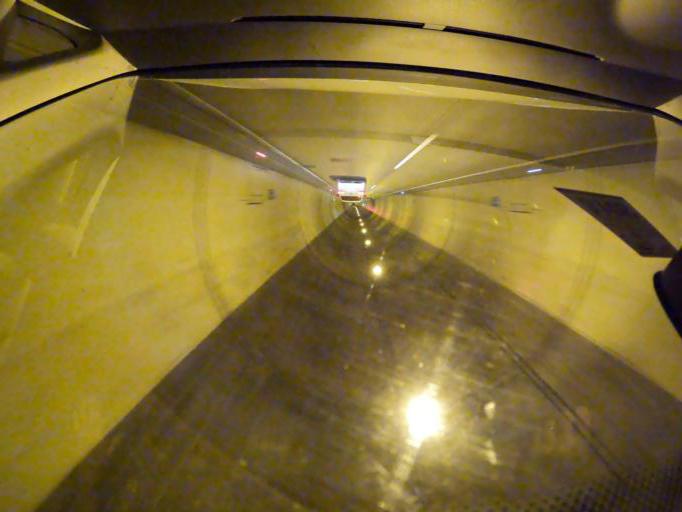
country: AT
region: Styria
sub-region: Politischer Bezirk Voitsberg
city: Modriach
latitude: 46.9800
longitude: 15.0722
